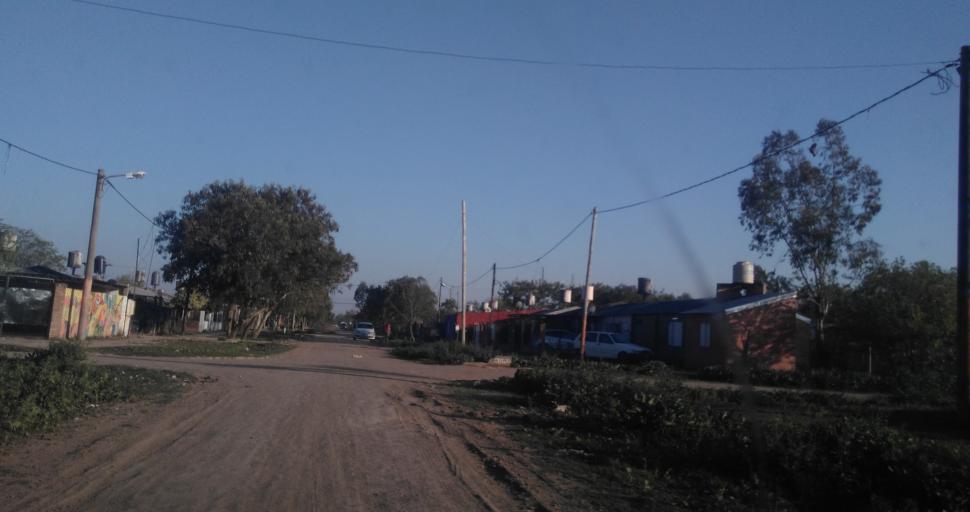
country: AR
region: Chaco
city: Resistencia
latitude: -27.4801
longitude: -59.0061
